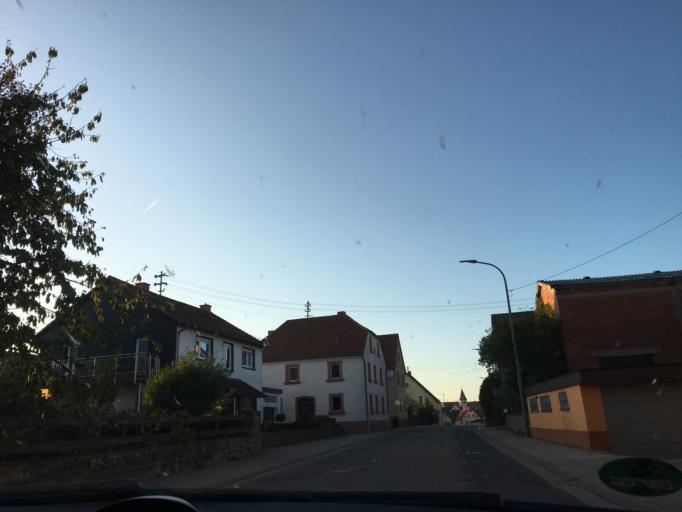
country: DE
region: Rheinland-Pfalz
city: Hermersberg
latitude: 49.3193
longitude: 7.6335
